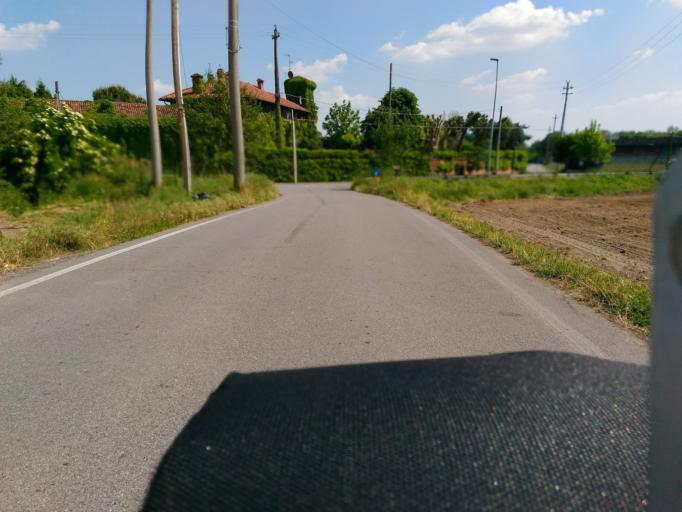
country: IT
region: Lombardy
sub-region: Citta metropolitana di Milano
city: Mombretto
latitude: 45.4110
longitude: 9.3585
